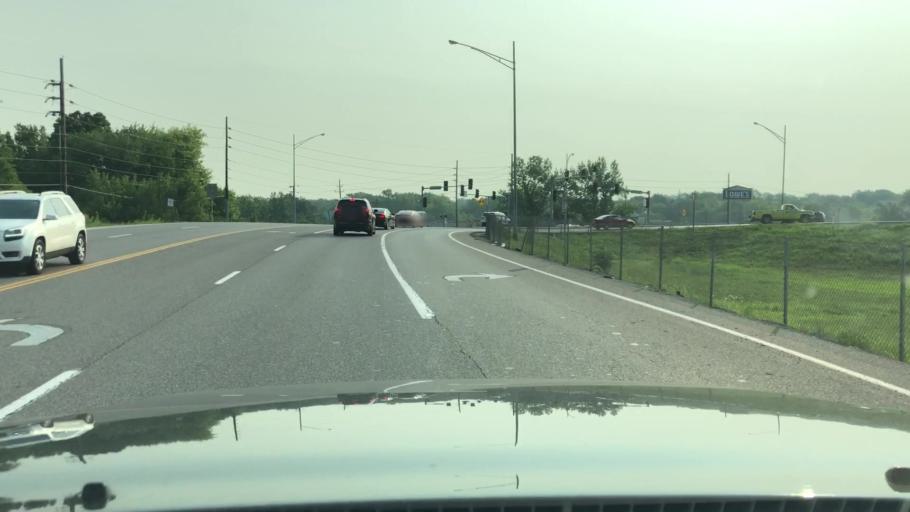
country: US
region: Missouri
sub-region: Saint Charles County
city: Saint Charles
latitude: 38.7878
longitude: -90.5341
